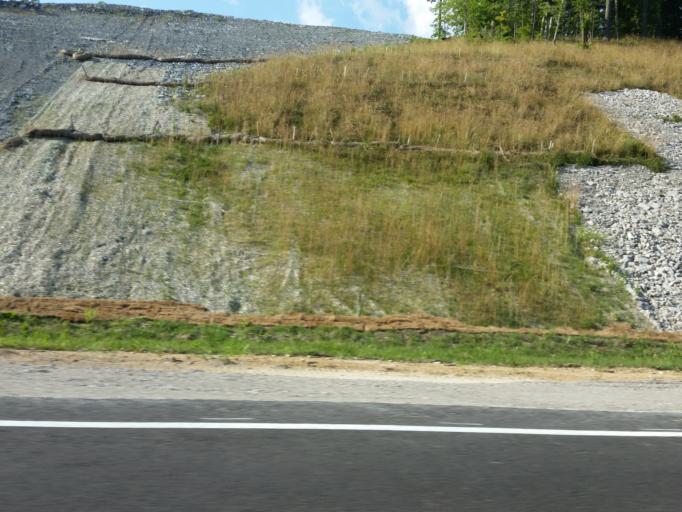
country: US
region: Tennessee
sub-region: Maury County
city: Mount Pleasant
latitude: 35.5649
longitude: -87.3558
